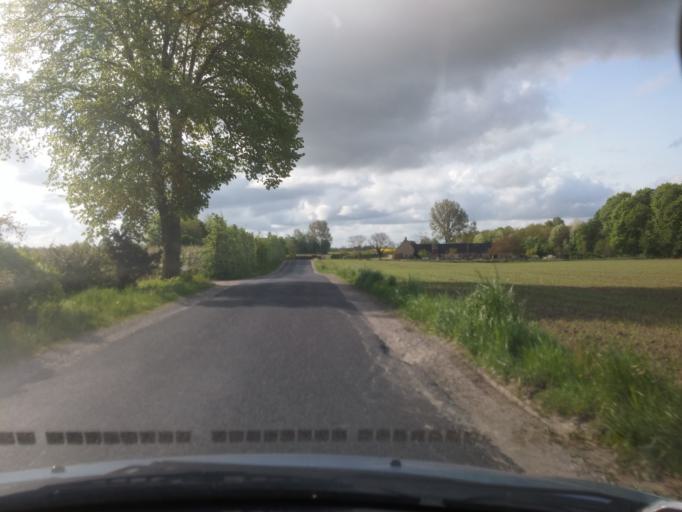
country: DK
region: South Denmark
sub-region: Nyborg Kommune
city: Ullerslev
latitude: 55.3767
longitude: 10.6460
